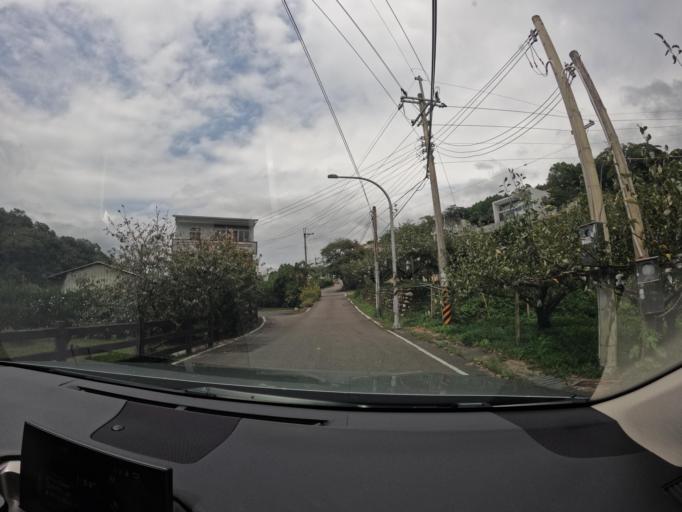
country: TW
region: Taiwan
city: Fengyuan
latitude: 24.3383
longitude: 120.8745
